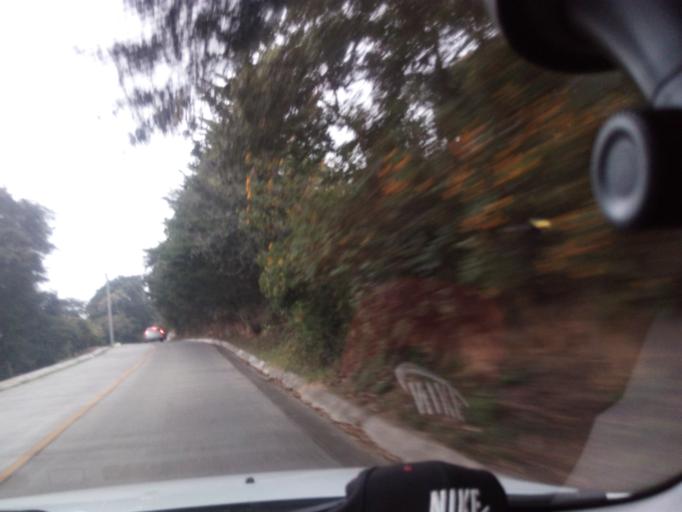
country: GT
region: Sacatepequez
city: Santa Lucia Milpas Altas
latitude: 14.5891
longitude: -90.7087
